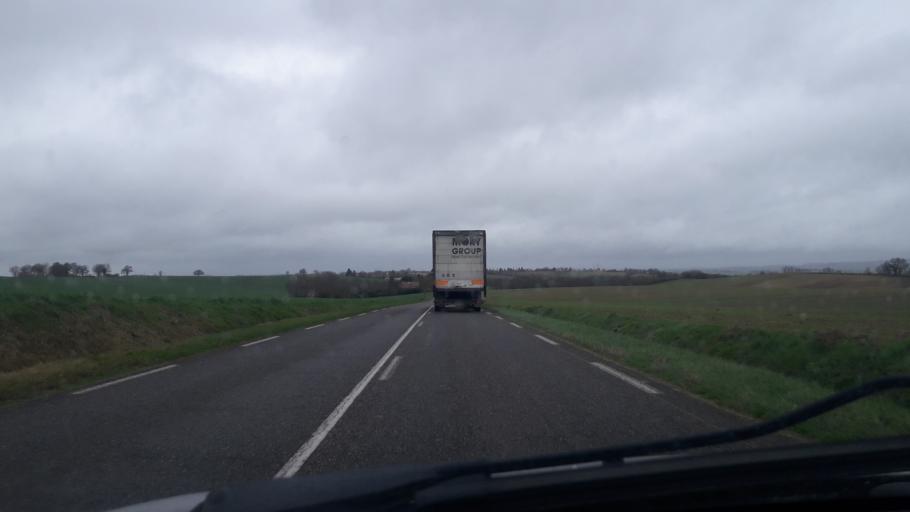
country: FR
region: Midi-Pyrenees
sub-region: Departement du Gers
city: Gimont
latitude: 43.7039
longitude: 0.9941
